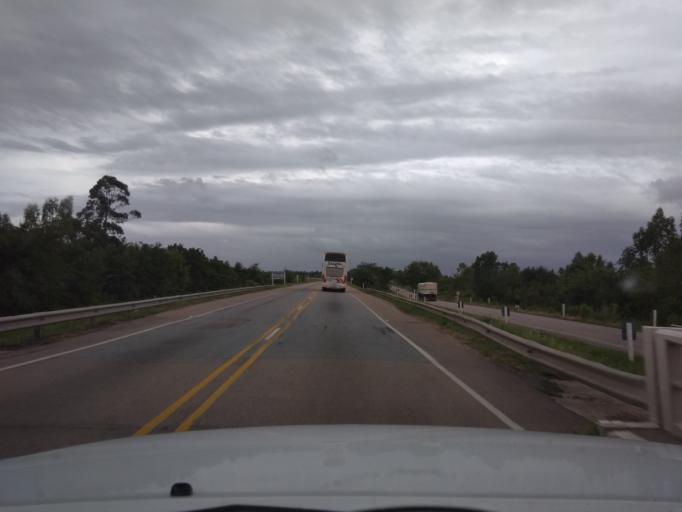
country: UY
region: Canelones
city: Canelones
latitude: -34.4991
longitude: -56.2819
